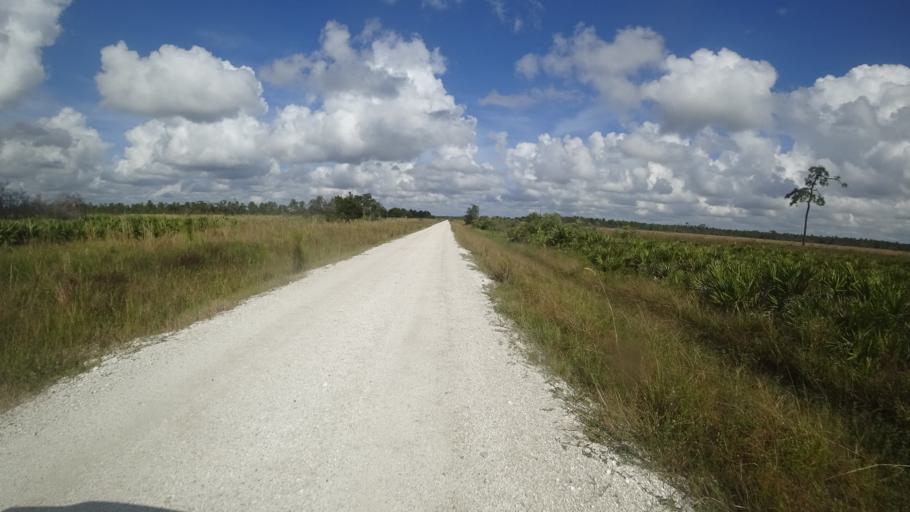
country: US
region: Florida
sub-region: Hillsborough County
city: Wimauma
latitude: 27.5280
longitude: -82.1280
